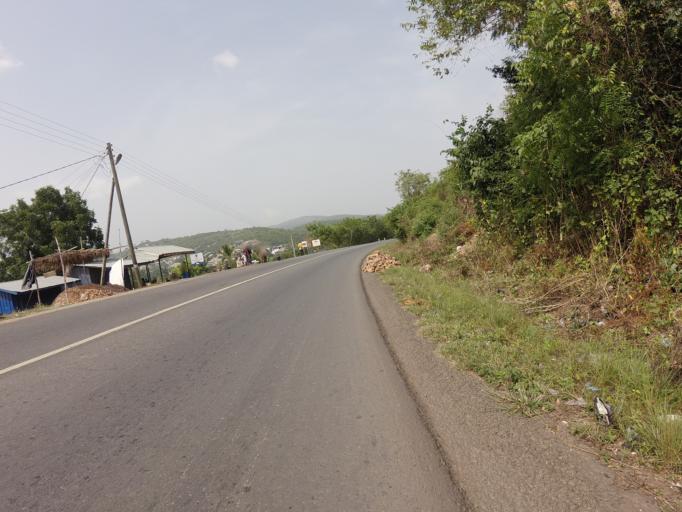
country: GH
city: Akropong
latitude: 6.2372
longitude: 0.1003
